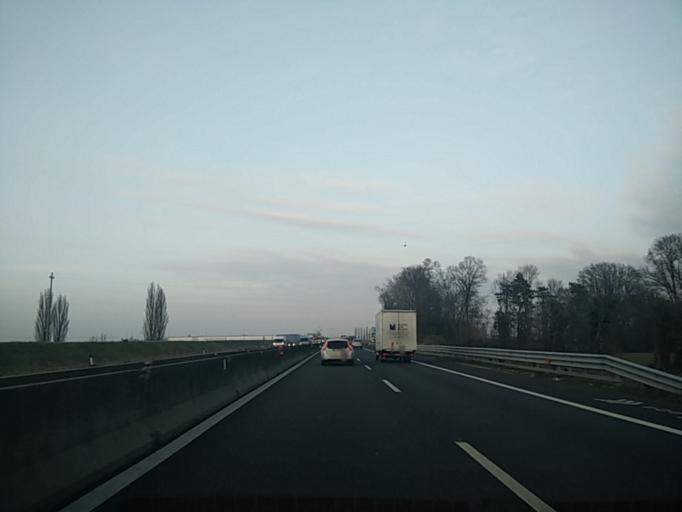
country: IT
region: Emilia-Romagna
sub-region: Provincia di Bologna
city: Bentivoglio
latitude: 44.6114
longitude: 11.4130
